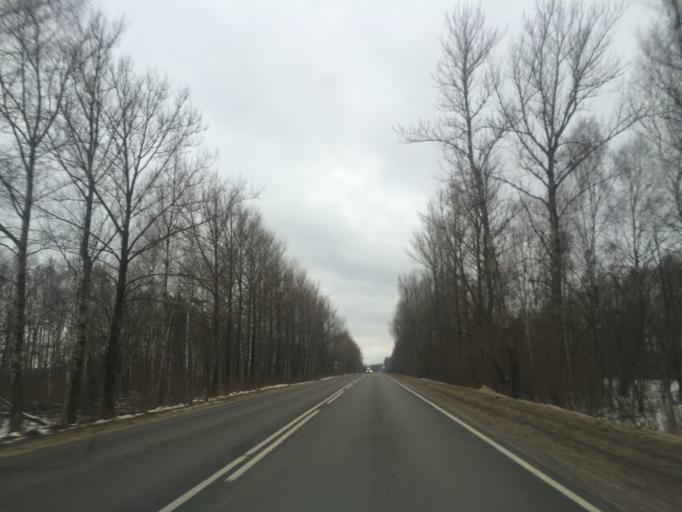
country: RU
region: Tula
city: Leninskiy
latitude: 54.1332
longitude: 37.2924
